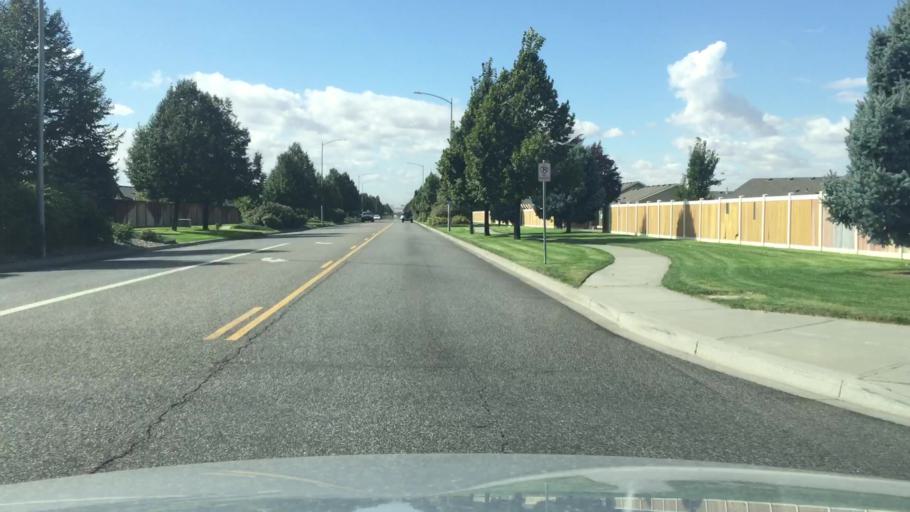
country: US
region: Washington
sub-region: Franklin County
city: West Pasco
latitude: 46.2780
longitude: -119.1944
